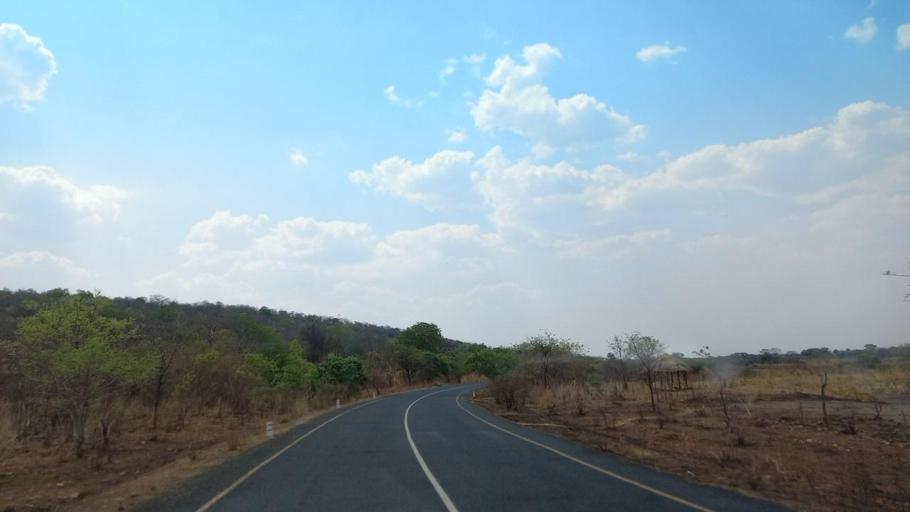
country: ZM
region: Lusaka
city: Luangwa
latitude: -15.3261
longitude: 30.3428
